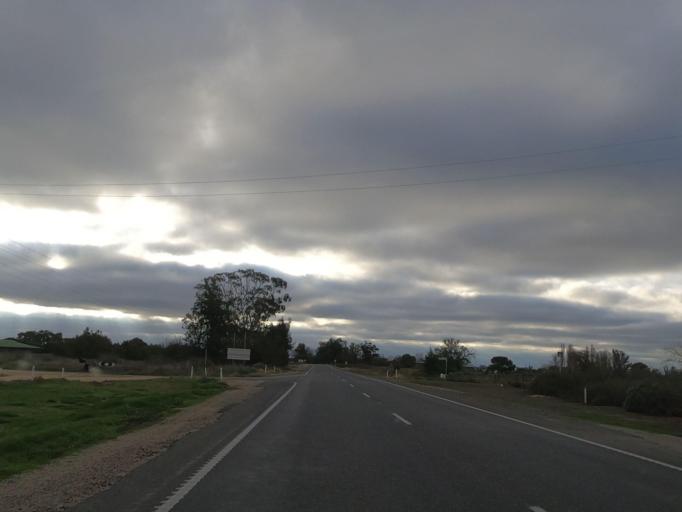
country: AU
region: Victoria
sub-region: Swan Hill
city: Swan Hill
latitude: -35.7272
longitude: 143.8911
